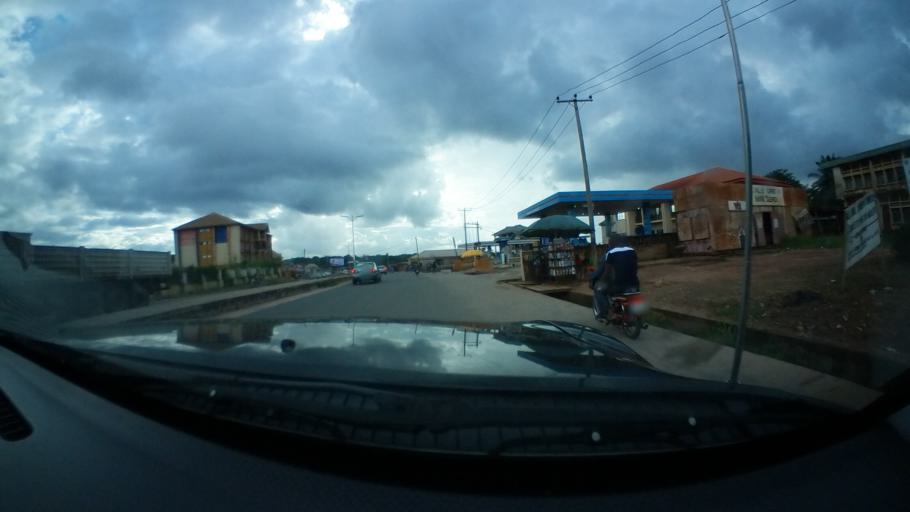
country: NG
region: Imo
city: Orlu
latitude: 5.7996
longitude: 7.0339
